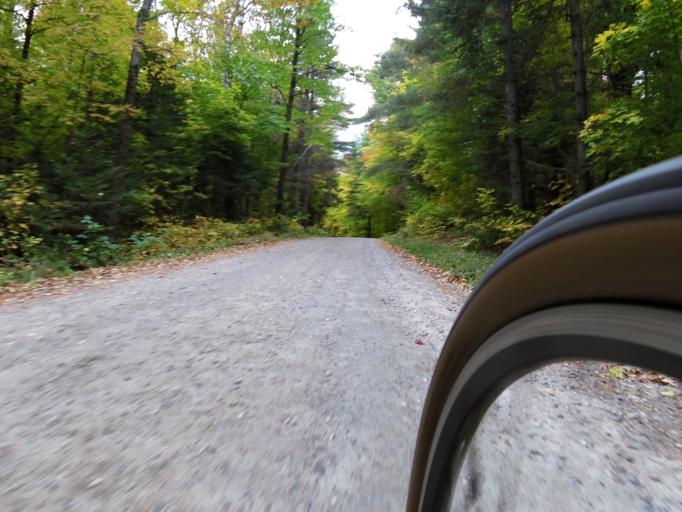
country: CA
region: Quebec
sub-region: Outaouais
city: Wakefield
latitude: 45.6021
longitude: -76.0347
